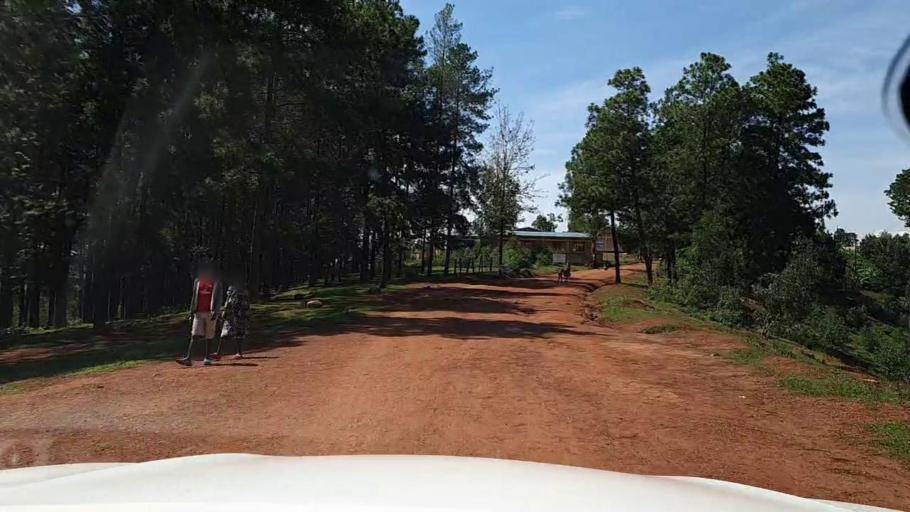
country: RW
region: Southern Province
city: Butare
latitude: -2.7163
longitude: 29.8394
